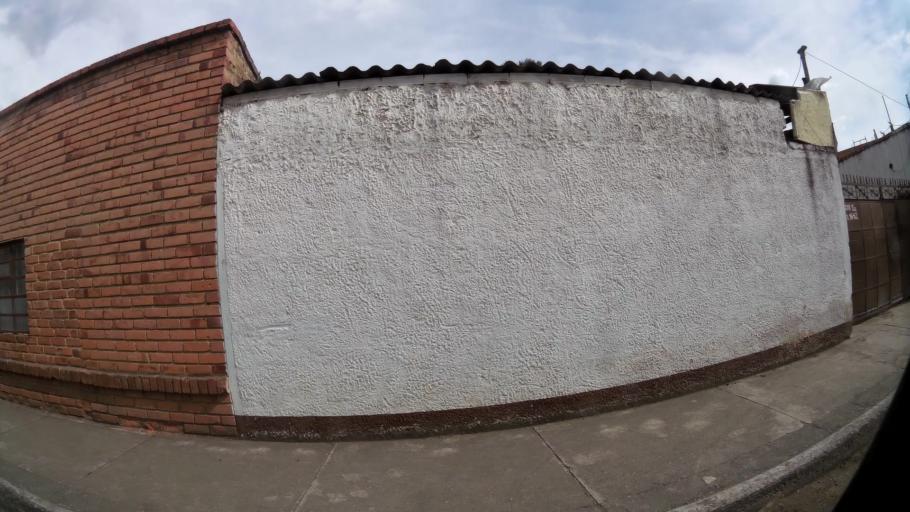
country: CO
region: Cundinamarca
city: Funza
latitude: 4.7060
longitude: -74.2030
